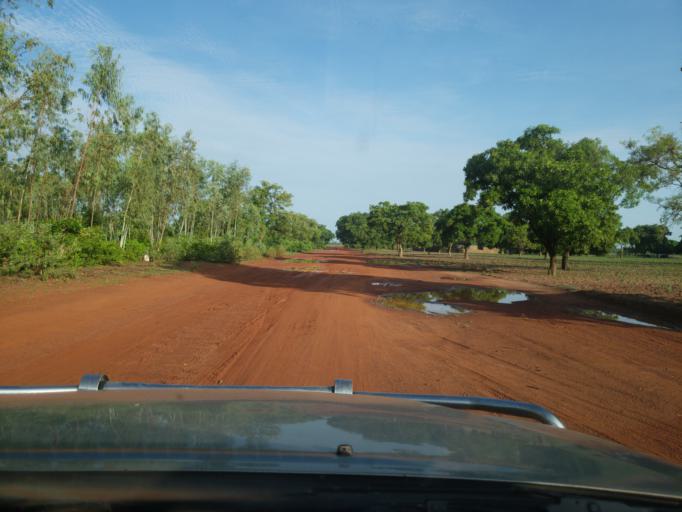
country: ML
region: Sikasso
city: Koutiala
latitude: 12.4272
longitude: -5.6001
